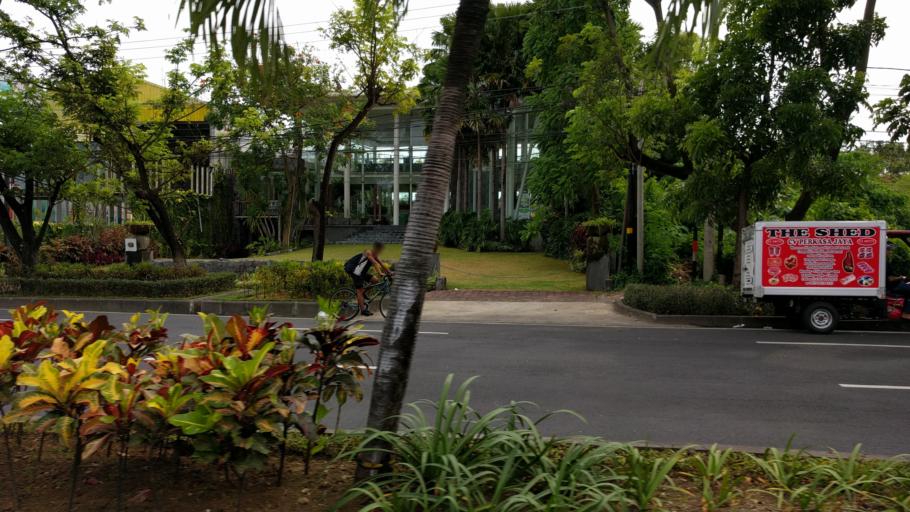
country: ID
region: Bali
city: Kuta
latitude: -8.6866
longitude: 115.1707
